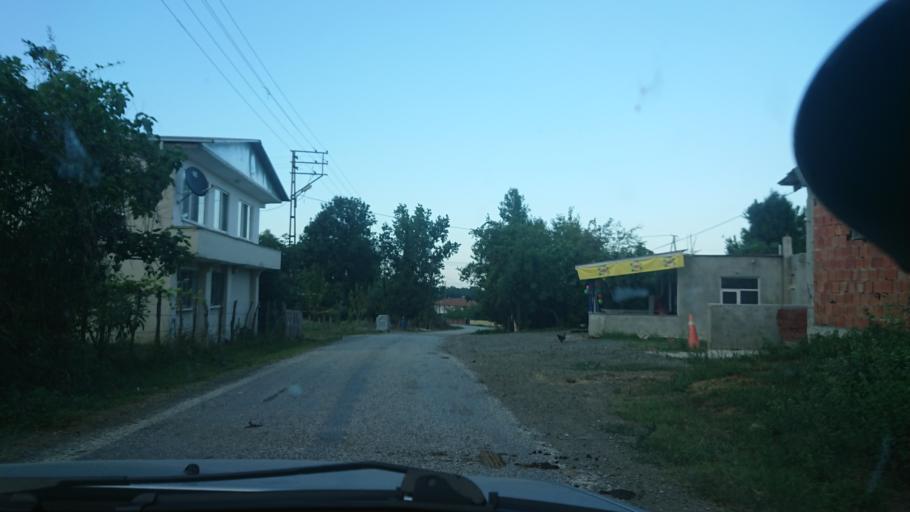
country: TR
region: Samsun
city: Dikbiyik
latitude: 41.1765
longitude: 36.5434
